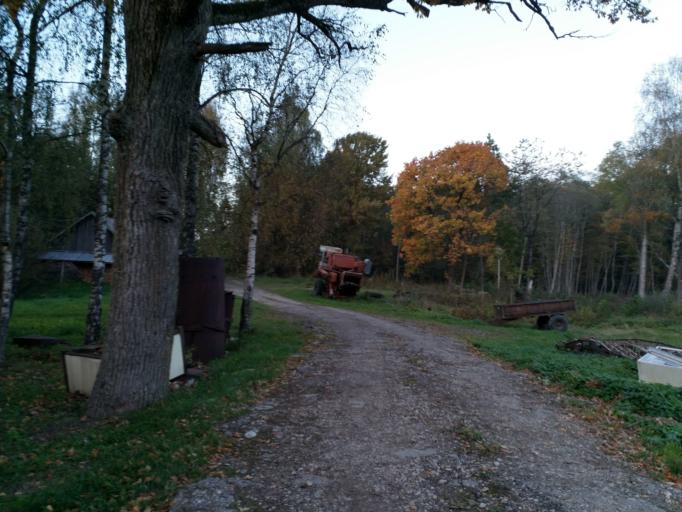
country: LV
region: Aizpute
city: Aizpute
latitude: 56.8369
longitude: 21.7741
